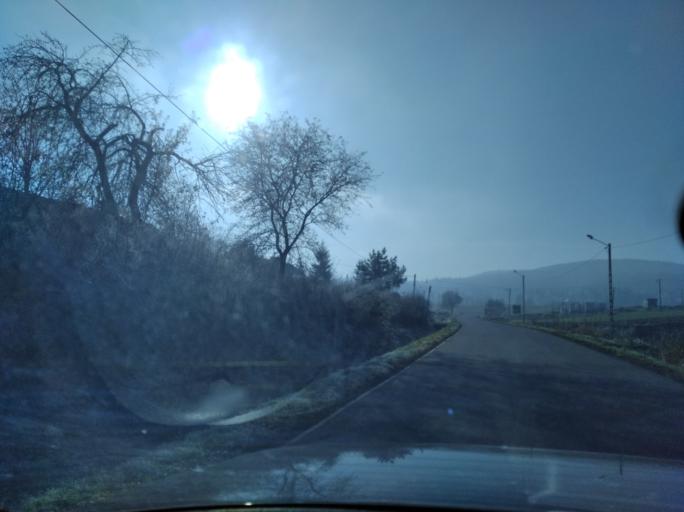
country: PL
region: Subcarpathian Voivodeship
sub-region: Powiat strzyzowski
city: Wysoka Strzyzowska
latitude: 49.8501
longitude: 21.7010
